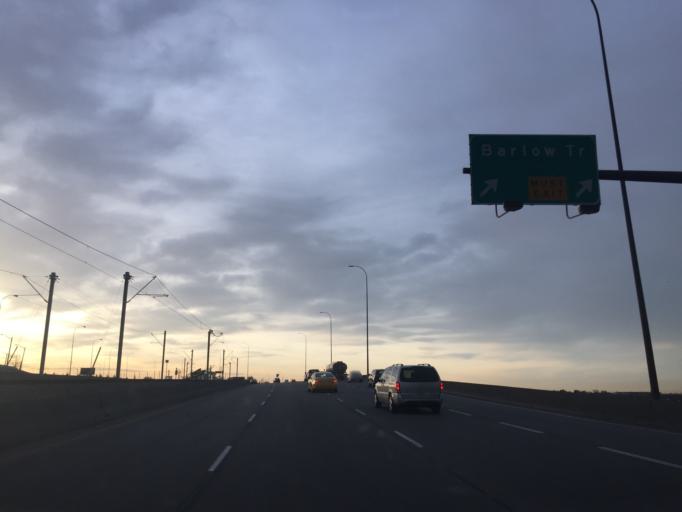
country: CA
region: Alberta
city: Calgary
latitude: 51.0465
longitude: -114.0104
